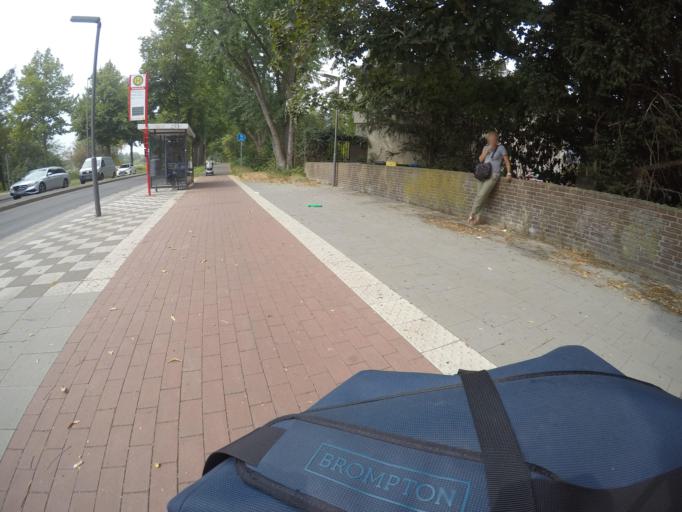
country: DE
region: North Rhine-Westphalia
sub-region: Regierungsbezirk Dusseldorf
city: Neuss
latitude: 51.1789
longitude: 6.7372
